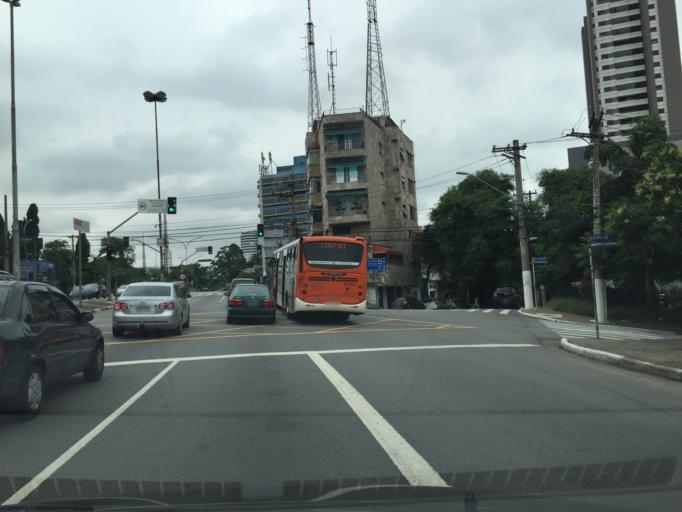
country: BR
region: Sao Paulo
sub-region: Sao Paulo
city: Sao Paulo
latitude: -23.5518
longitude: -46.6766
